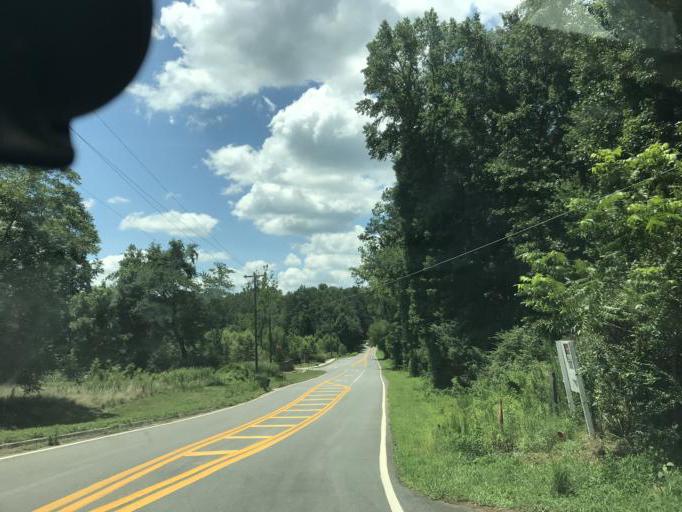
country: US
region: Georgia
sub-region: Fulton County
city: Milton
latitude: 34.2188
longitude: -84.2546
